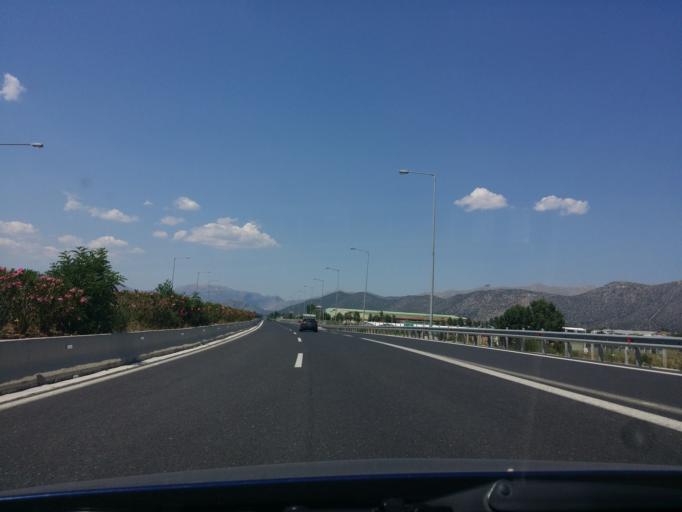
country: GR
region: Peloponnese
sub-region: Nomos Arkadias
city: Tripoli
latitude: 37.5049
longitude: 22.4010
